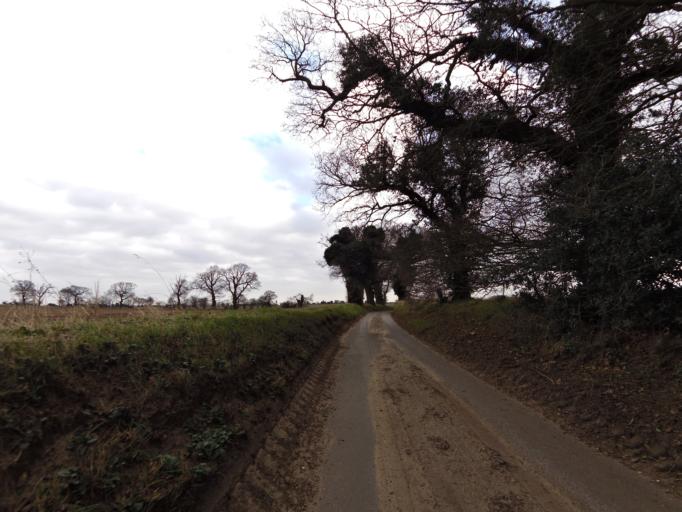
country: GB
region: England
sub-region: Suffolk
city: Woodbridge
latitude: 52.0433
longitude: 1.3209
